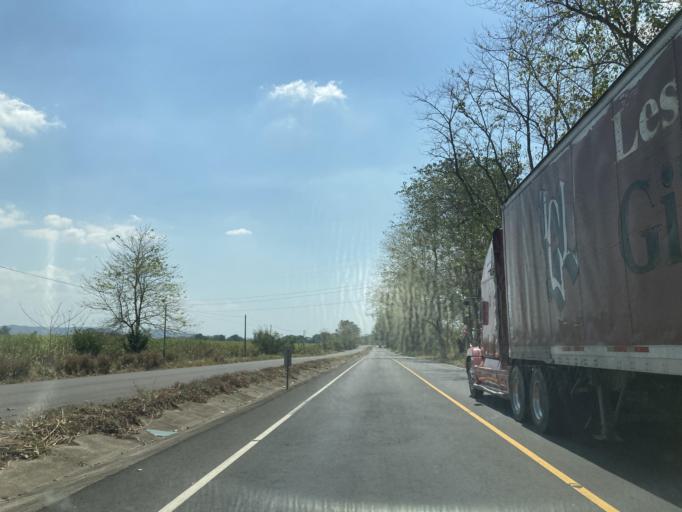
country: GT
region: Escuintla
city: Guanagazapa
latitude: 14.1976
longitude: -90.6991
